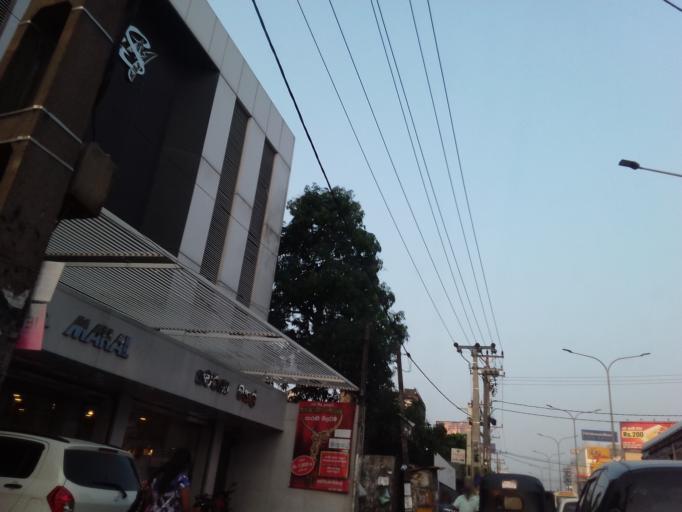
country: LK
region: Western
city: Kelaniya
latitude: 6.9758
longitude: 79.9248
